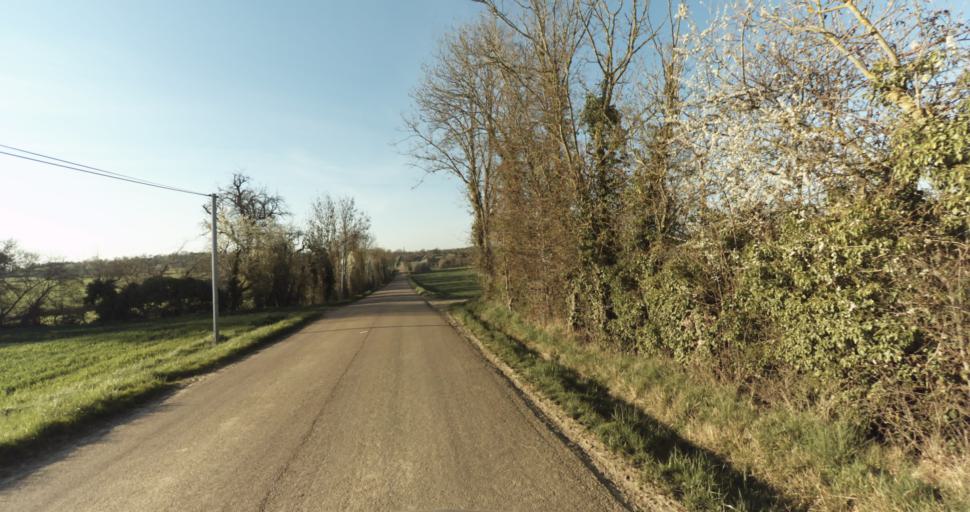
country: FR
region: Lower Normandy
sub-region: Departement du Calvados
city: Saint-Pierre-sur-Dives
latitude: 48.9436
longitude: 0.0175
